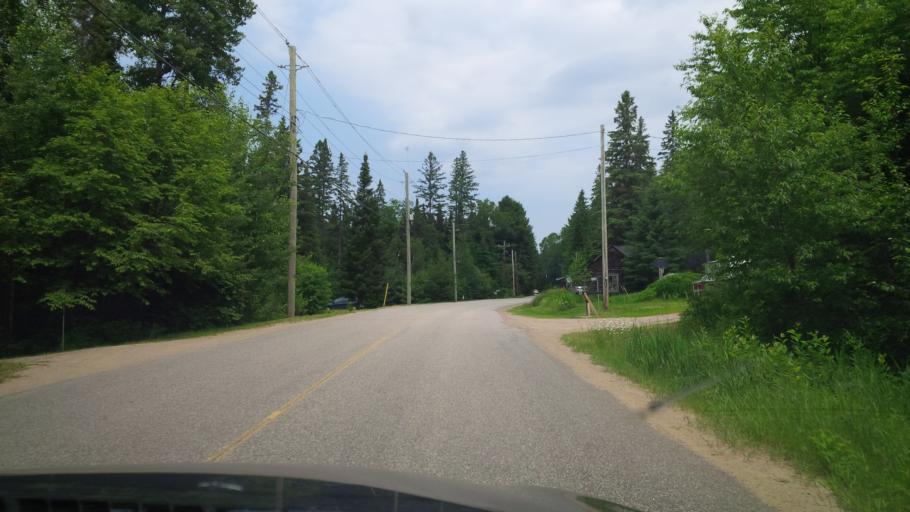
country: CA
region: Ontario
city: Huntsville
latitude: 45.6174
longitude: -79.1576
